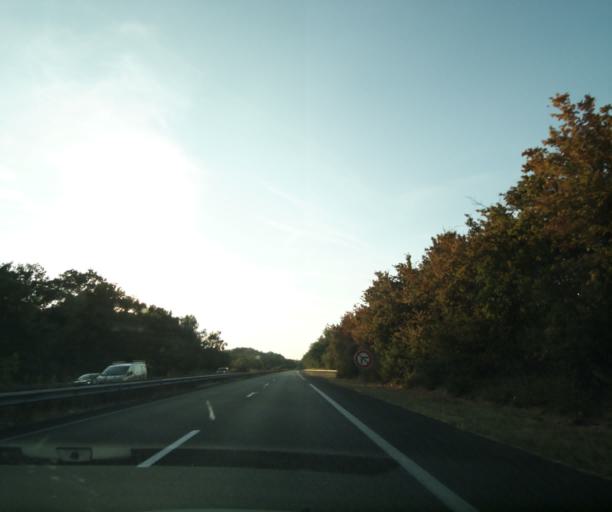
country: FR
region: Aquitaine
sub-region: Departement du Lot-et-Garonne
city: Layrac
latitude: 44.1257
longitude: 0.6978
